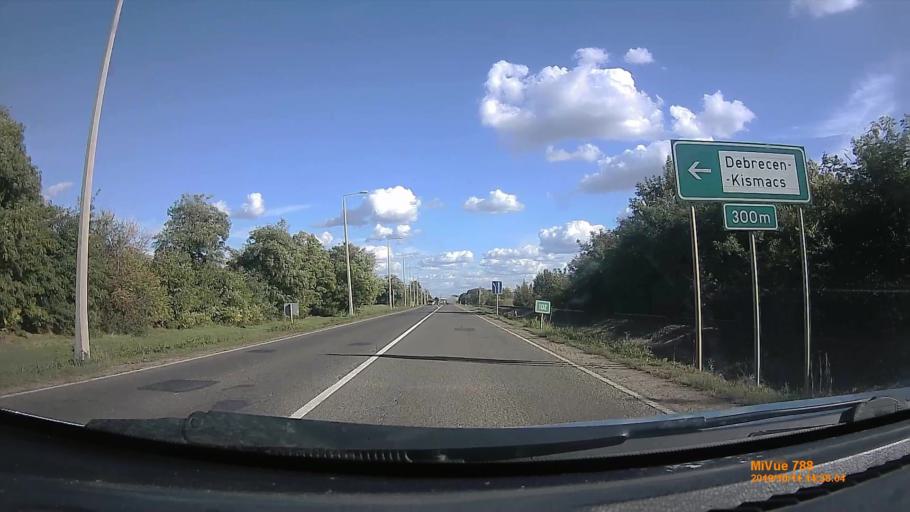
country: HU
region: Hajdu-Bihar
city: Ebes
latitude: 47.5520
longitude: 21.5366
